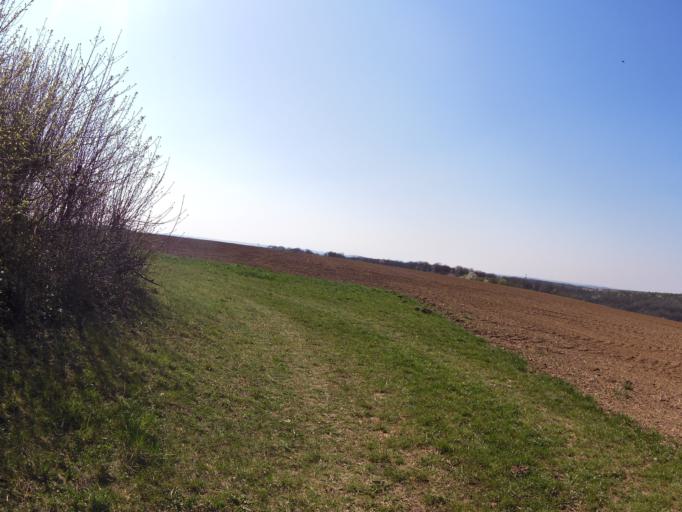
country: DE
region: Bavaria
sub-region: Regierungsbezirk Unterfranken
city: Rottendorf
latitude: 49.8162
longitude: 10.0759
